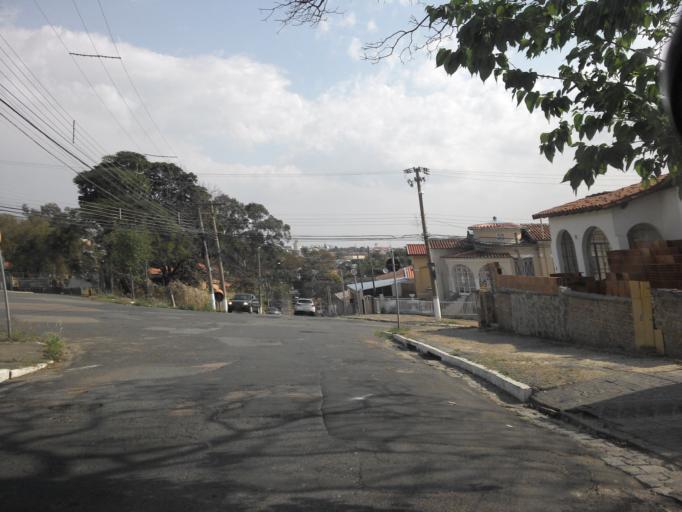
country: BR
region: Sao Paulo
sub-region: Campinas
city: Campinas
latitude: -22.9120
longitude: -47.0672
